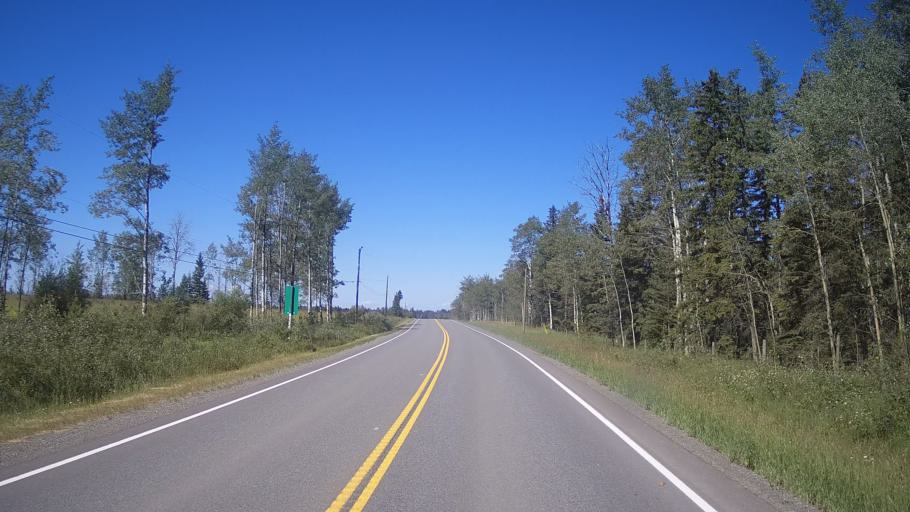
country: CA
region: British Columbia
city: Cache Creek
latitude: 51.5450
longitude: -120.9439
